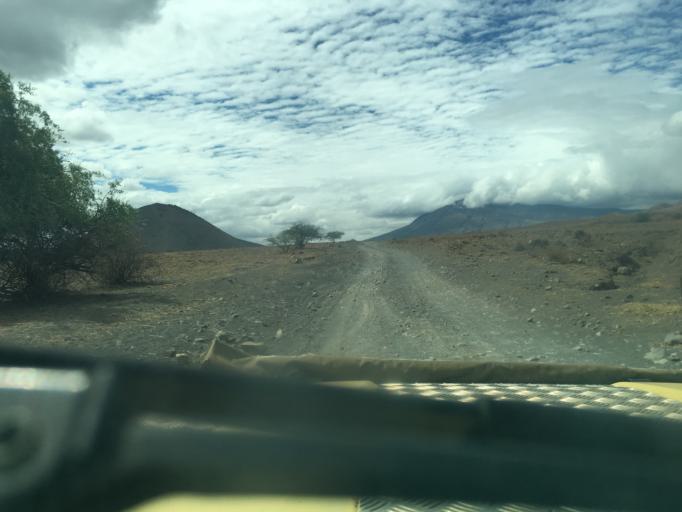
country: TZ
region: Arusha
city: Mto wa Mbu
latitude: -2.7308
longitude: 35.9684
